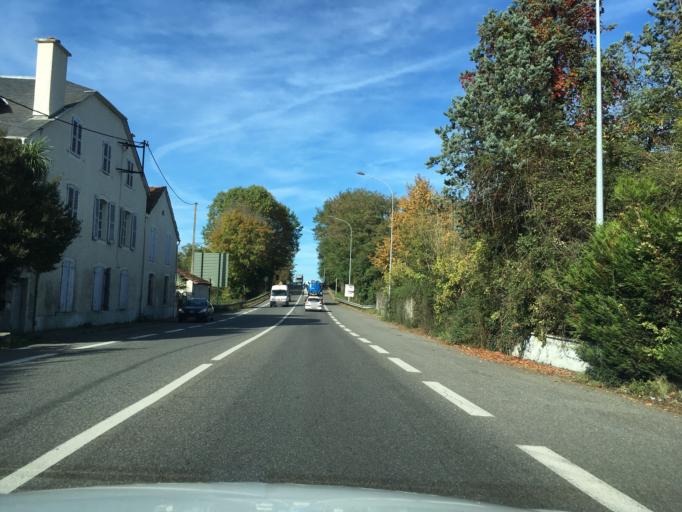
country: FR
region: Aquitaine
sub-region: Departement des Pyrenees-Atlantiques
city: Lons
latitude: 43.3401
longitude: -0.3798
